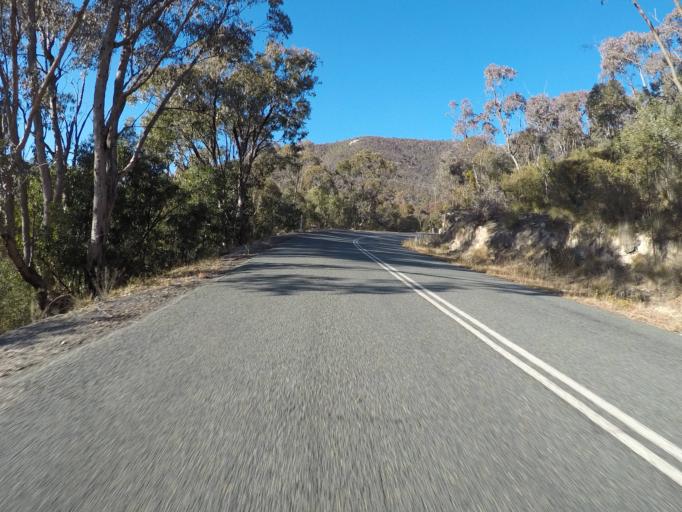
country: AU
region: Australian Capital Territory
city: Macarthur
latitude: -35.4791
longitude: 148.9469
